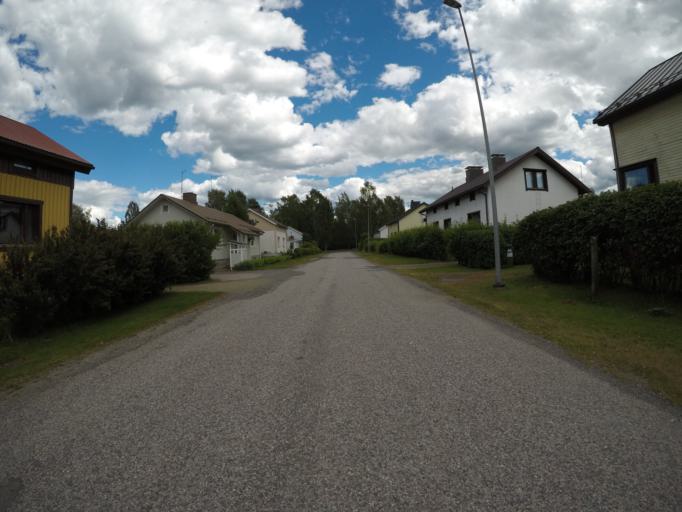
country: FI
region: Haeme
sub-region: Haemeenlinna
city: Haemeenlinna
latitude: 60.9956
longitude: 24.4385
